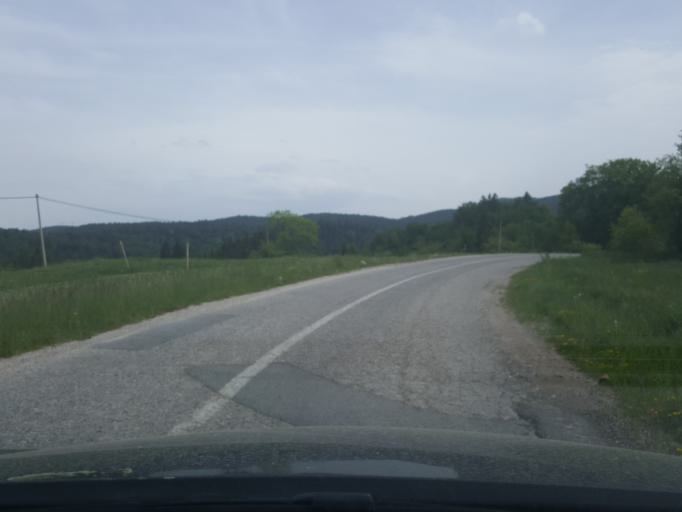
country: RS
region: Central Serbia
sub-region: Zlatiborski Okrug
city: Bajina Basta
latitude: 43.8986
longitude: 19.5198
